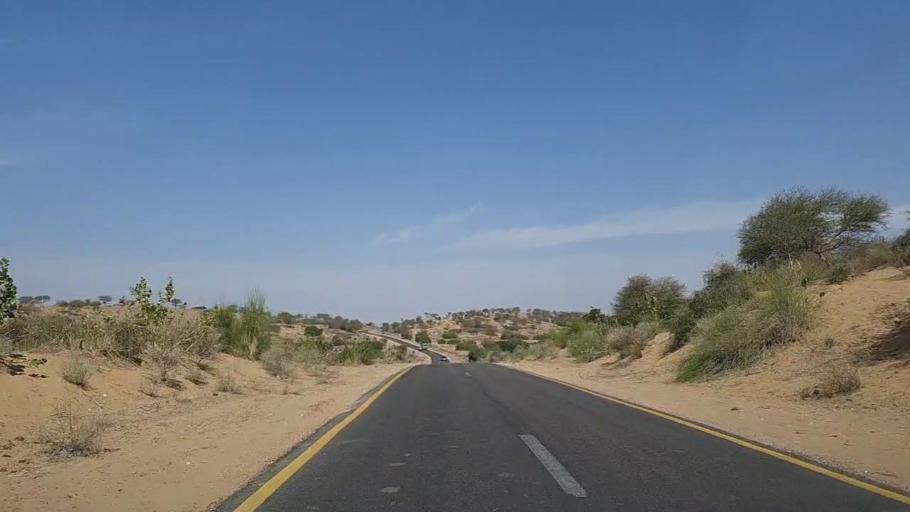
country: PK
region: Sindh
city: Mithi
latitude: 24.9057
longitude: 69.8884
